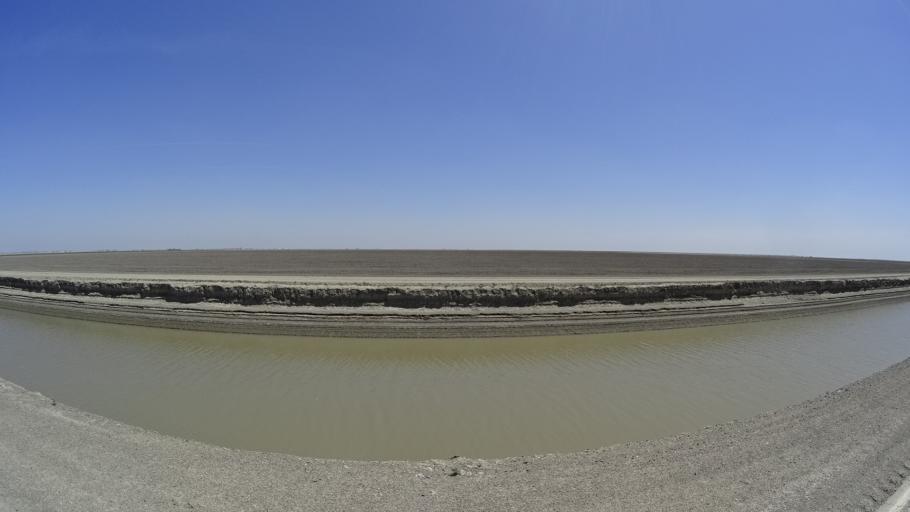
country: US
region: California
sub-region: Kings County
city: Corcoran
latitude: 35.9961
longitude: -119.6432
